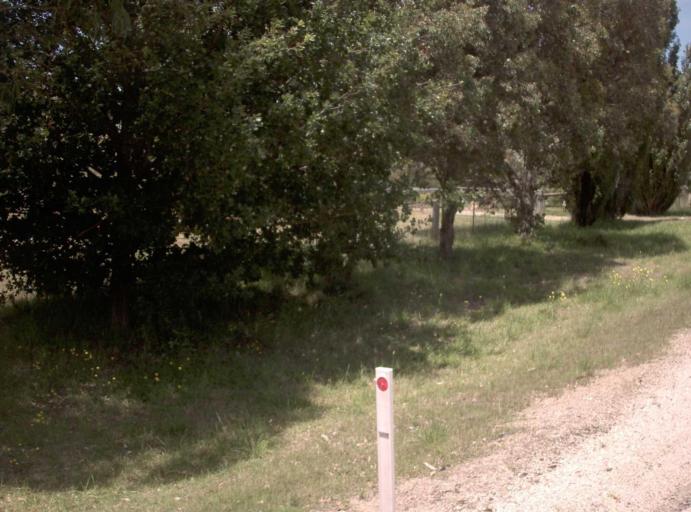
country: AU
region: Victoria
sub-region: East Gippsland
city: Bairnsdale
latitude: -37.5034
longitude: 147.8408
